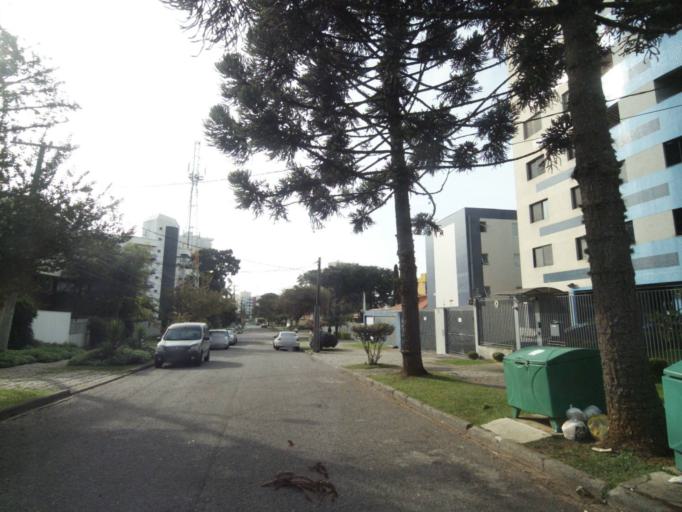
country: BR
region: Parana
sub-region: Curitiba
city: Curitiba
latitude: -25.4198
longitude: -49.2587
